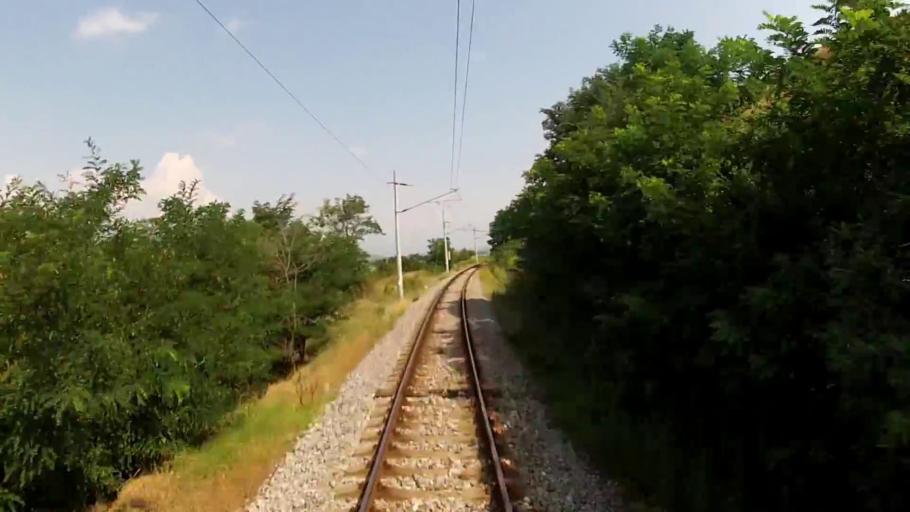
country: BG
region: Blagoevgrad
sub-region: Obshtina Sandanski
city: Sandanski
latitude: 41.5689
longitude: 23.2426
